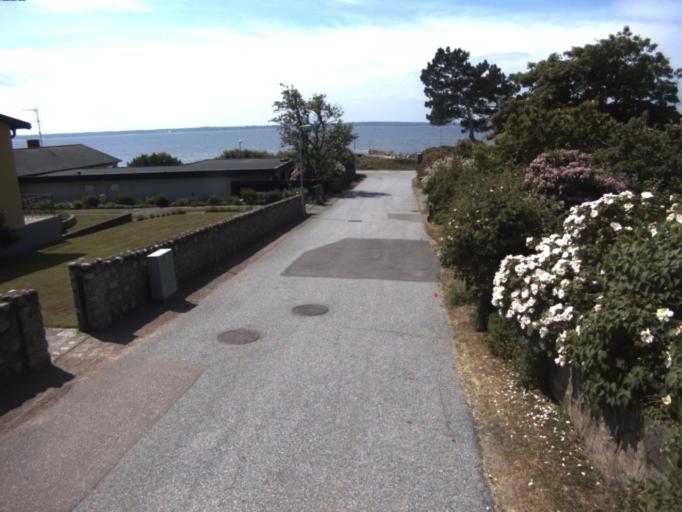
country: DK
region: Capital Region
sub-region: Helsingor Kommune
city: Hellebaek
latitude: 56.1219
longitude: 12.6022
